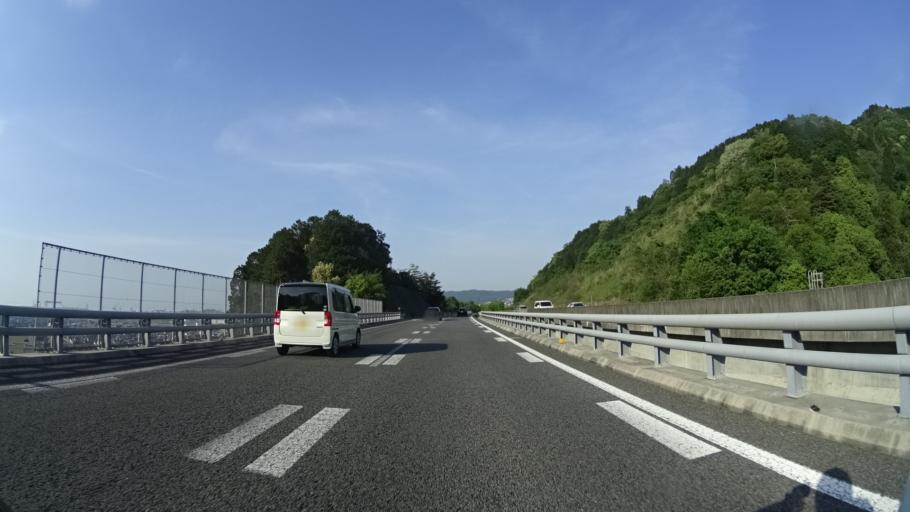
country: JP
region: Ehime
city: Saijo
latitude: 33.9024
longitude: 133.2016
